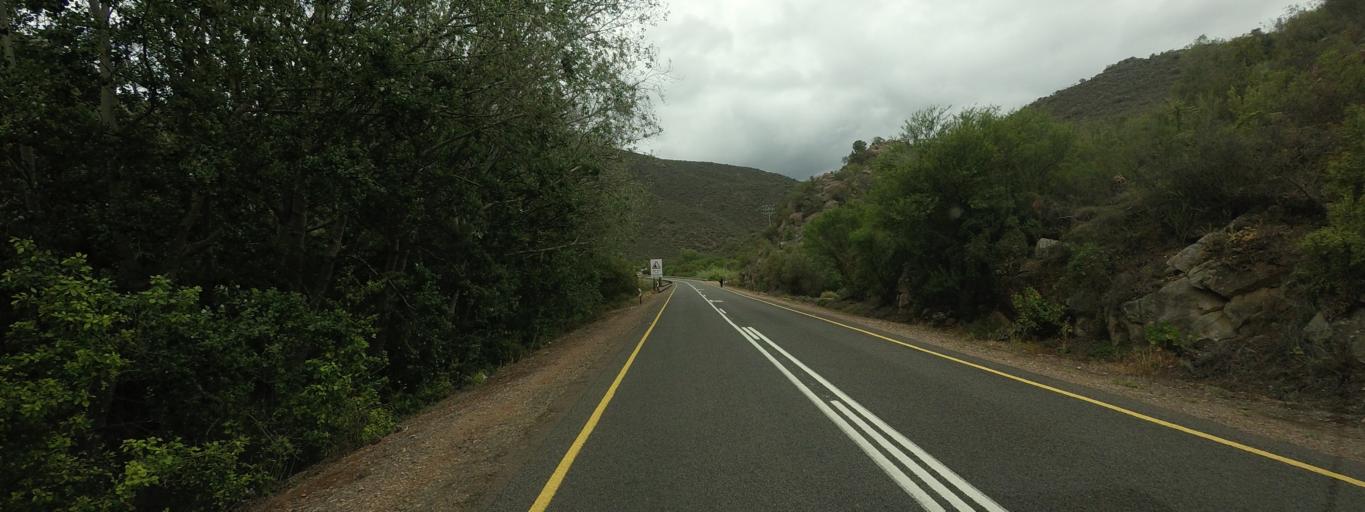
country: ZA
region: Western Cape
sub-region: Eden District Municipality
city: Oudtshoorn
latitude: -33.4649
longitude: 22.2546
